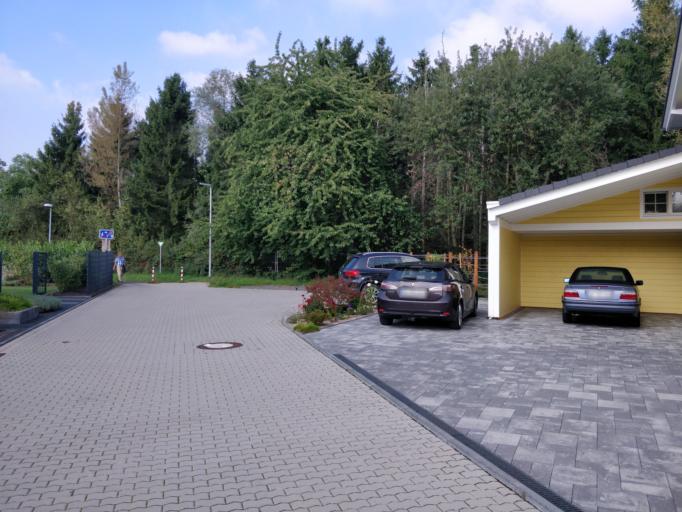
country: DE
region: North Rhine-Westphalia
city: Sankt Augustin
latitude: 50.7584
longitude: 7.1575
